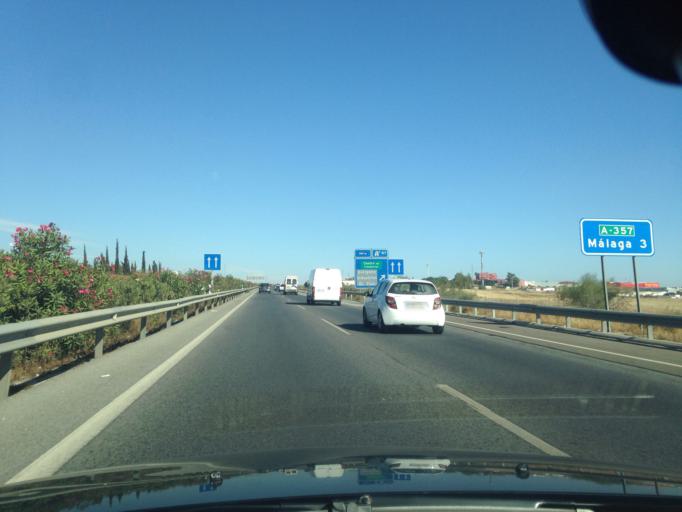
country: ES
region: Andalusia
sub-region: Provincia de Malaga
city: Malaga
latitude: 36.7138
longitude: -4.4968
